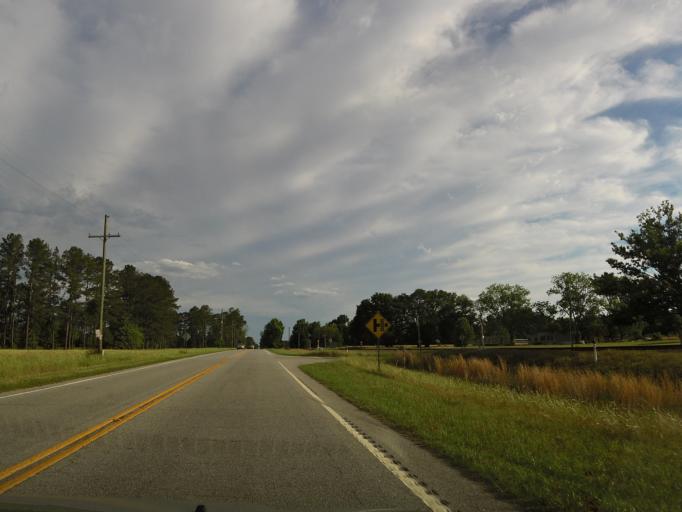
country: US
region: South Carolina
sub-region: Hampton County
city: Estill
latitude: 32.6729
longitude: -81.2433
